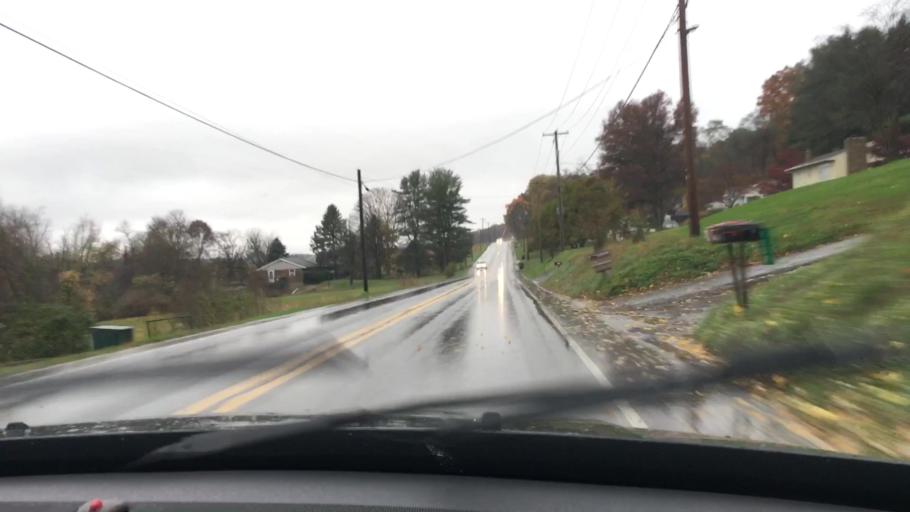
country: US
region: Pennsylvania
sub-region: Lancaster County
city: Quarryville
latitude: 39.8663
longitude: -76.2539
